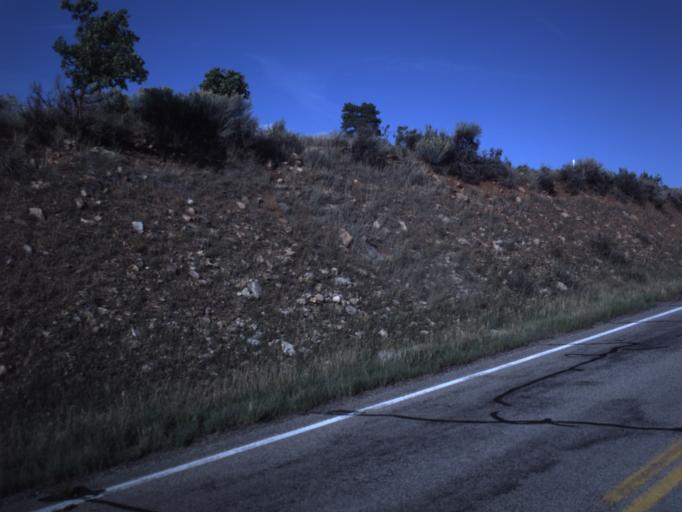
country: US
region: Utah
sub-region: Grand County
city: Moab
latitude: 38.3448
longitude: -109.1919
